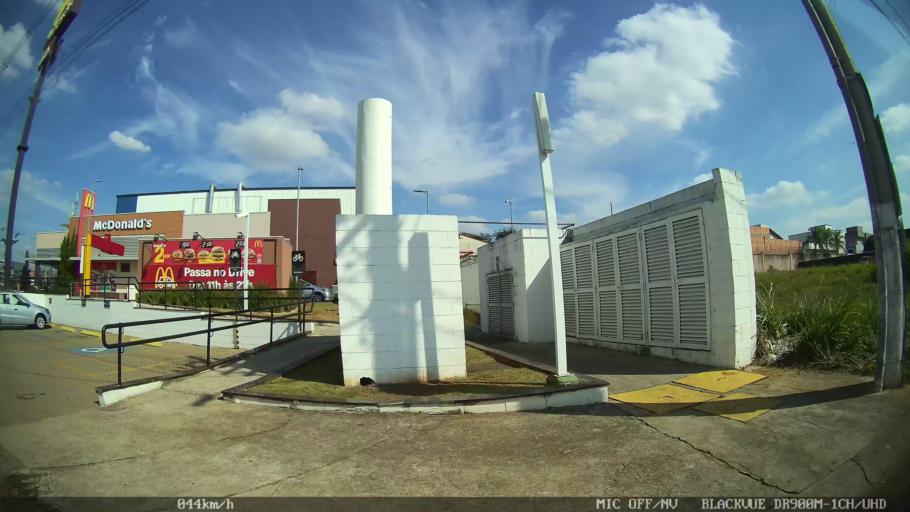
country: BR
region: Sao Paulo
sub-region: Hortolandia
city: Hortolandia
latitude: -22.8678
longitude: -47.2260
